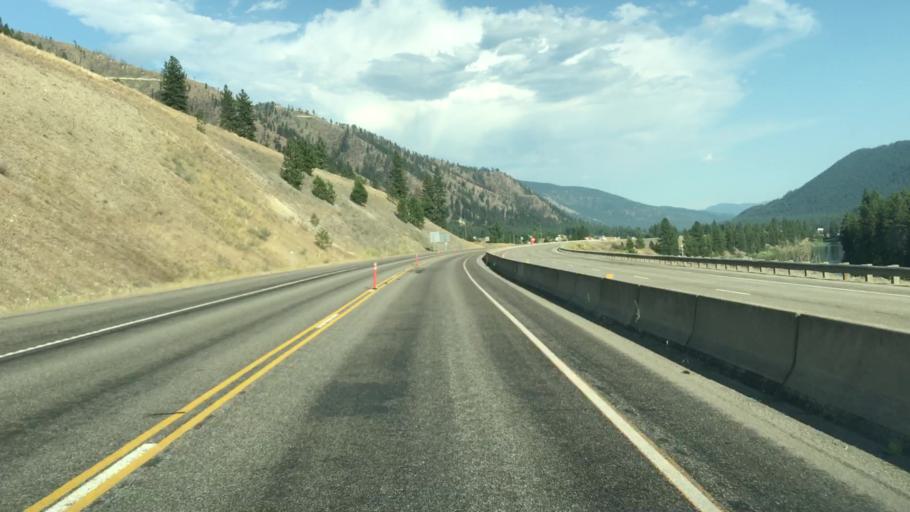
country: US
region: Montana
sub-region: Mineral County
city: Superior
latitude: 47.2166
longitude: -114.9505
